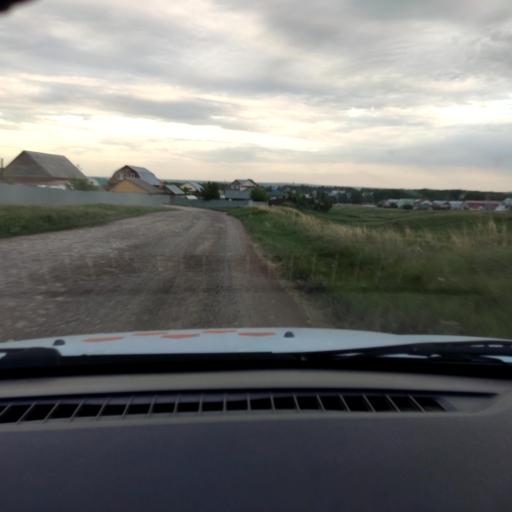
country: RU
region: Bashkortostan
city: Chishmy
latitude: 54.6092
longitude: 55.3958
